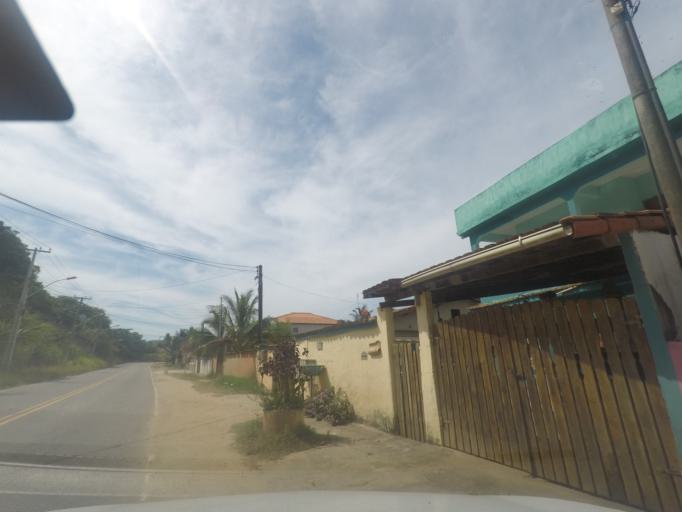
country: BR
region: Rio de Janeiro
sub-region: Marica
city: Marica
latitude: -22.9462
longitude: -42.6985
